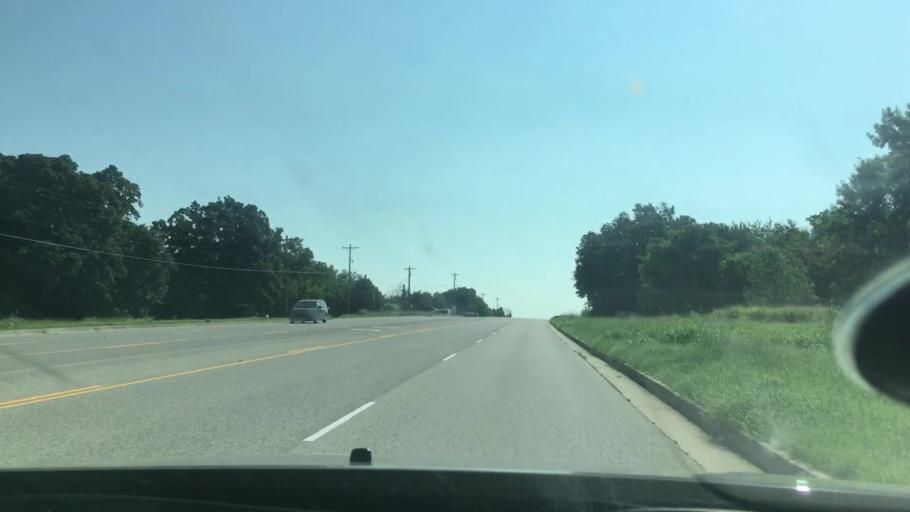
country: US
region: Oklahoma
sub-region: Marshall County
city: Oakland
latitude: 34.1000
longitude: -96.8014
